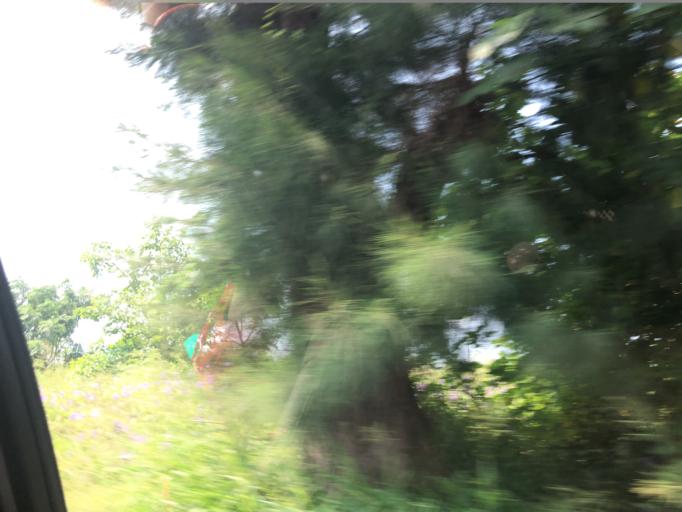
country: TW
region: Taiwan
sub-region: Chiayi
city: Taibao
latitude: 23.4620
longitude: 120.1508
